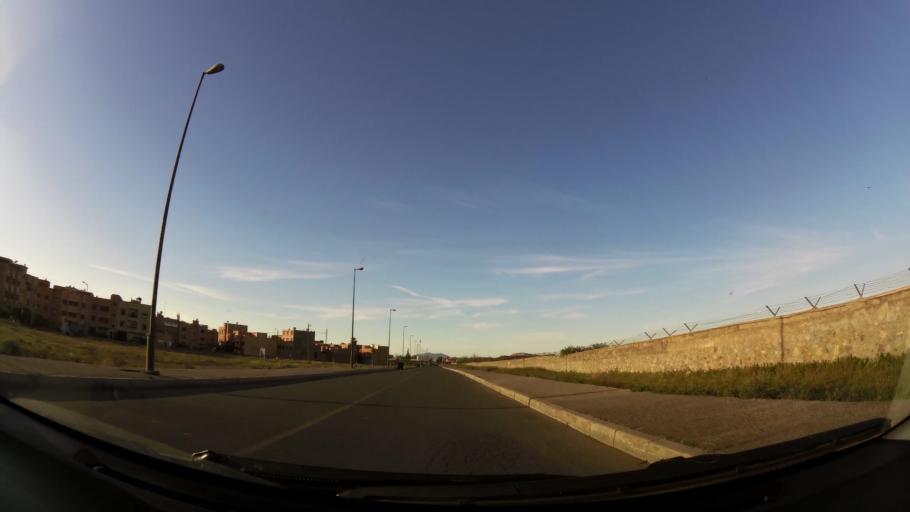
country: MA
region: Marrakech-Tensift-Al Haouz
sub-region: Marrakech
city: Marrakesh
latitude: 31.6177
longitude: -8.0449
